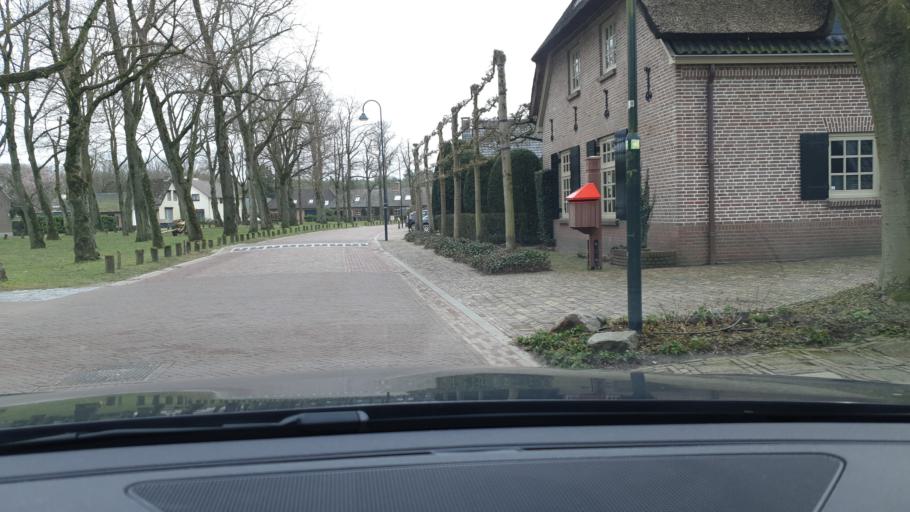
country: NL
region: North Brabant
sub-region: Gemeente Veldhoven
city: Oerle
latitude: 51.4147
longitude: 5.3584
